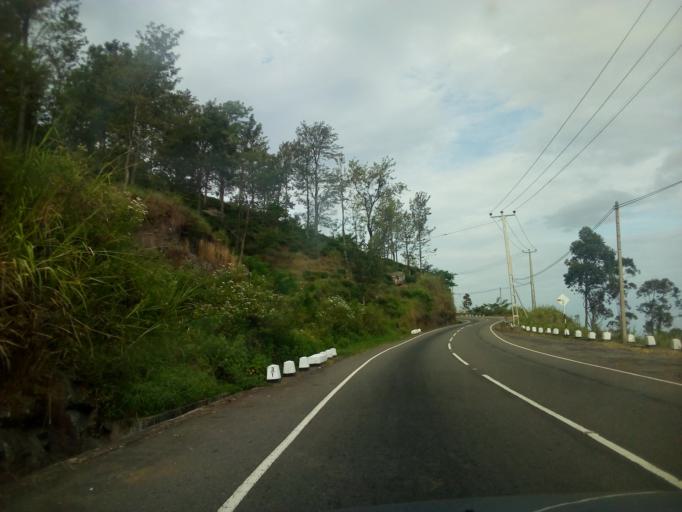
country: LK
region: Uva
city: Haputale
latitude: 6.7617
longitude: 80.9303
